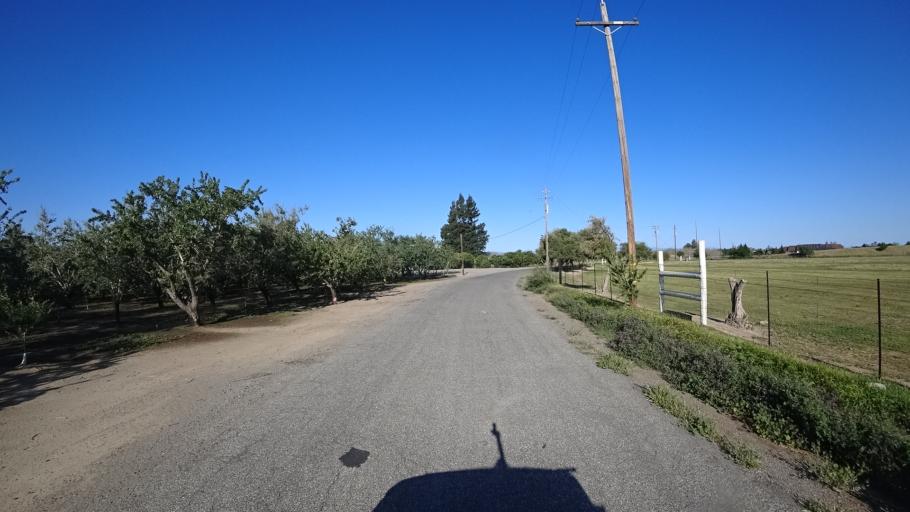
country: US
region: California
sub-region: Glenn County
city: Orland
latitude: 39.7181
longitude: -122.1705
